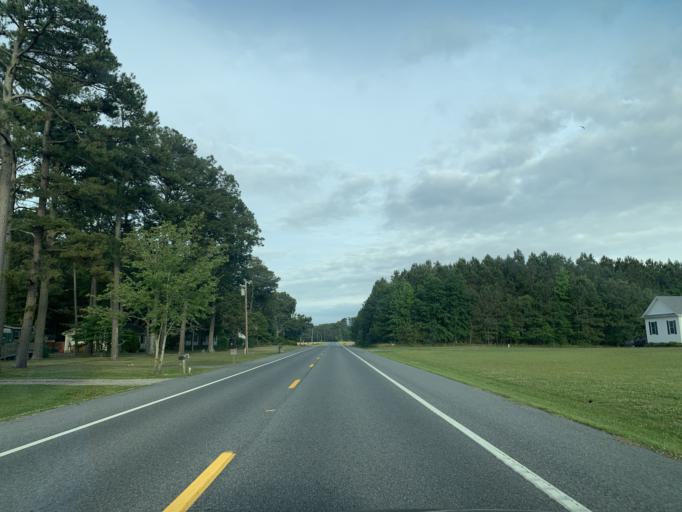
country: US
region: Virginia
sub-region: Accomack County
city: Captains Cove
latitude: 38.0711
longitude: -75.4706
